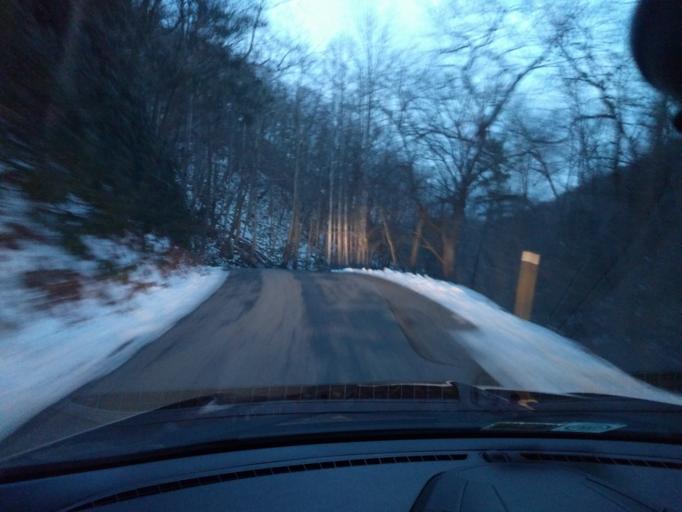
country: US
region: Virginia
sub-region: Alleghany County
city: Clifton Forge
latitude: 37.8540
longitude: -79.8589
